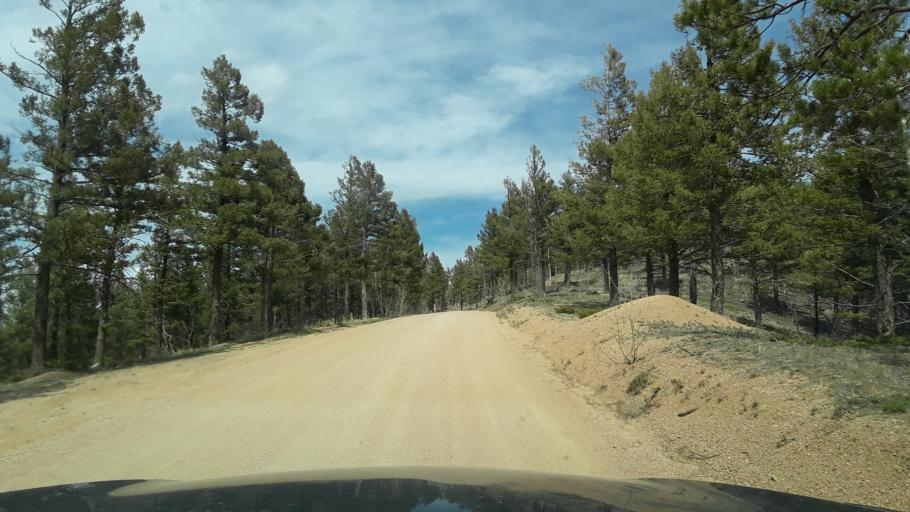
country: US
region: Colorado
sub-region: El Paso County
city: Palmer Lake
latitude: 39.0612
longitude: -104.9730
